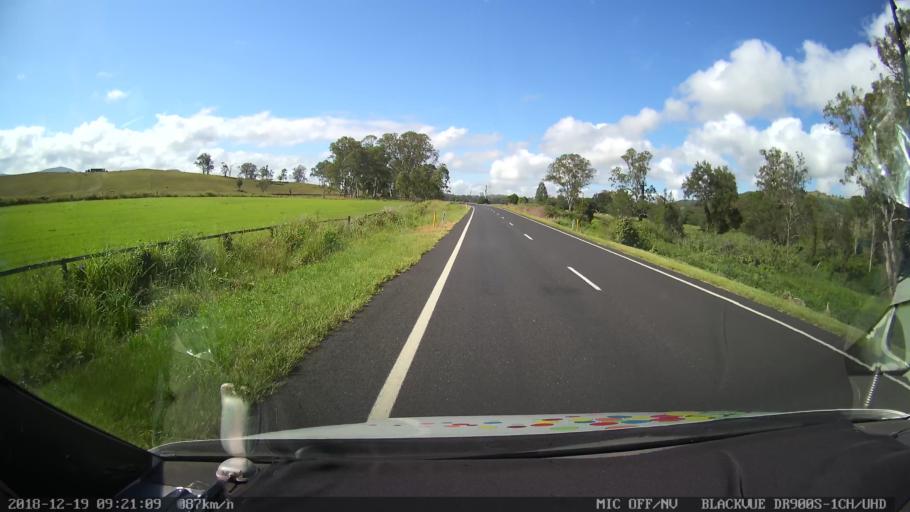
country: AU
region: New South Wales
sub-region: Kyogle
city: Kyogle
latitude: -28.5801
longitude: 152.9822
